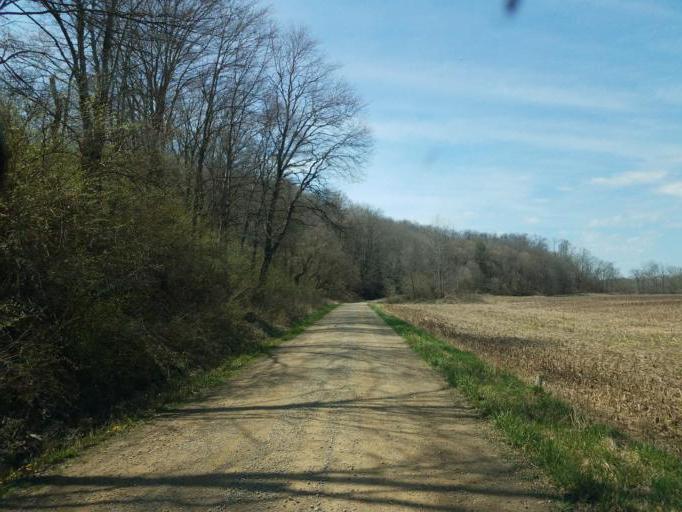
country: US
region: Ohio
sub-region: Knox County
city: Oak Hill
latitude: 40.3763
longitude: -82.2304
